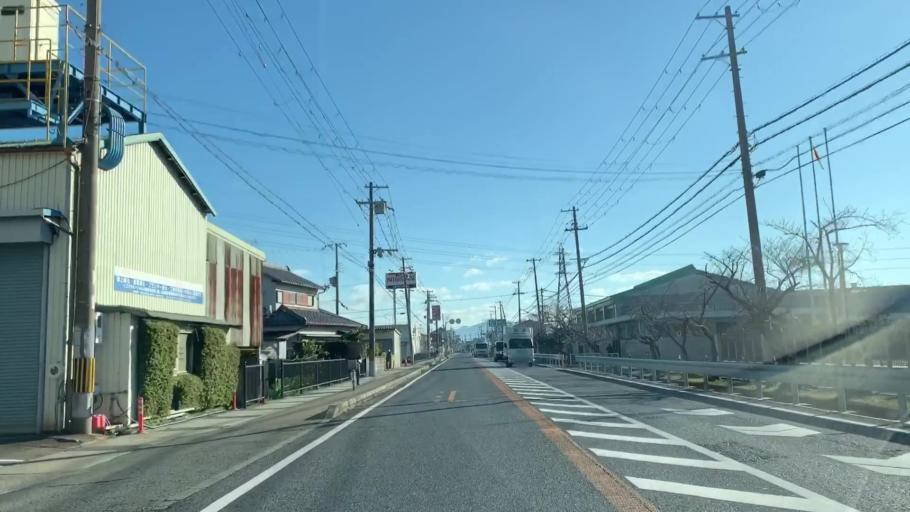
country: JP
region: Wakayama
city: Wakayama-shi
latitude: 34.2449
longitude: 135.2024
